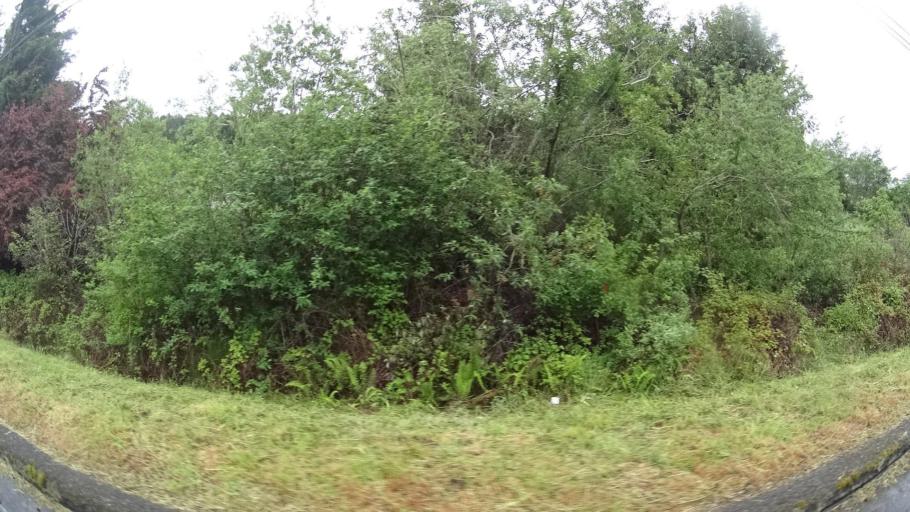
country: US
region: California
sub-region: Humboldt County
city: Bayside
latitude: 40.8376
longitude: -124.0537
